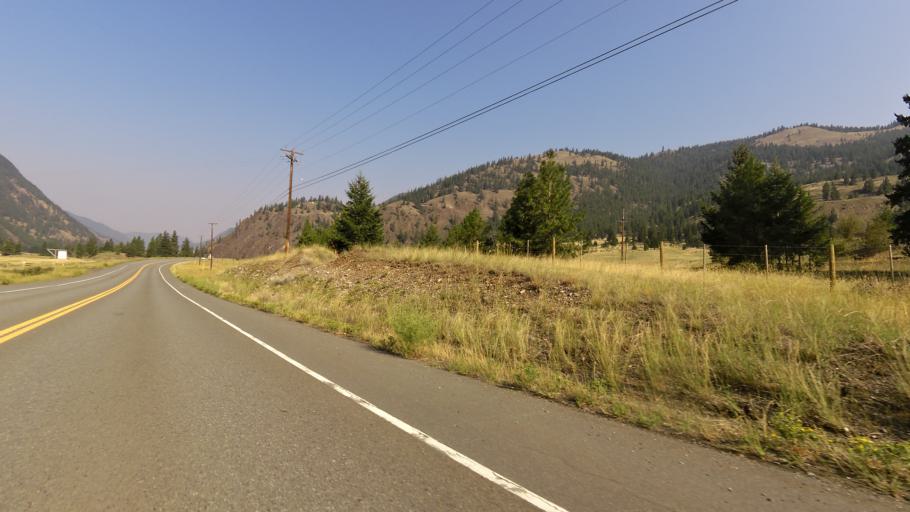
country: CA
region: British Columbia
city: Princeton
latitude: 49.3549
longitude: -120.0919
